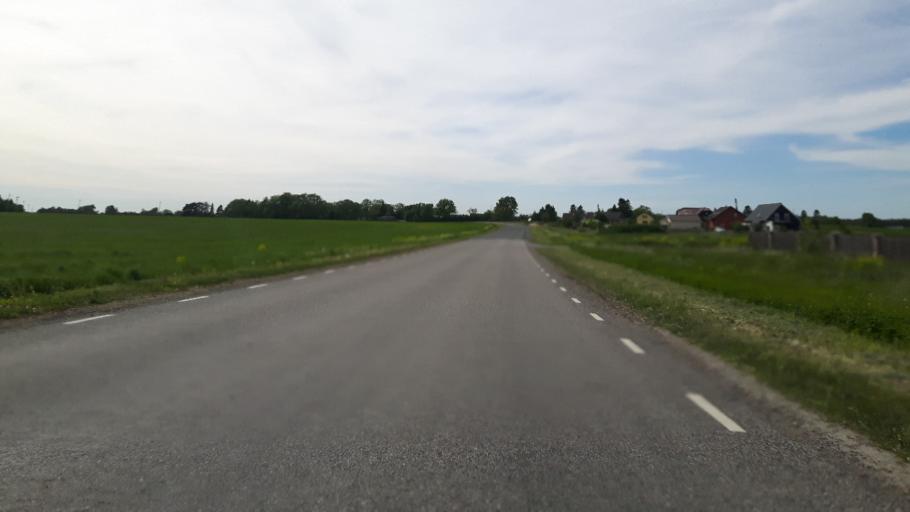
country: EE
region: Harju
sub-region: Joelaehtme vald
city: Loo
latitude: 59.4243
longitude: 24.9989
